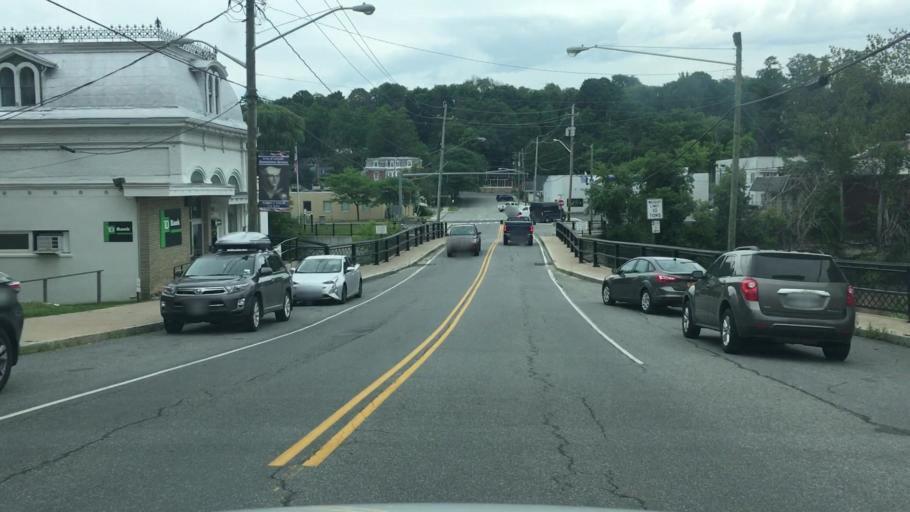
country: US
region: New York
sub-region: Essex County
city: Keeseville
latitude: 44.5054
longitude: -73.4815
